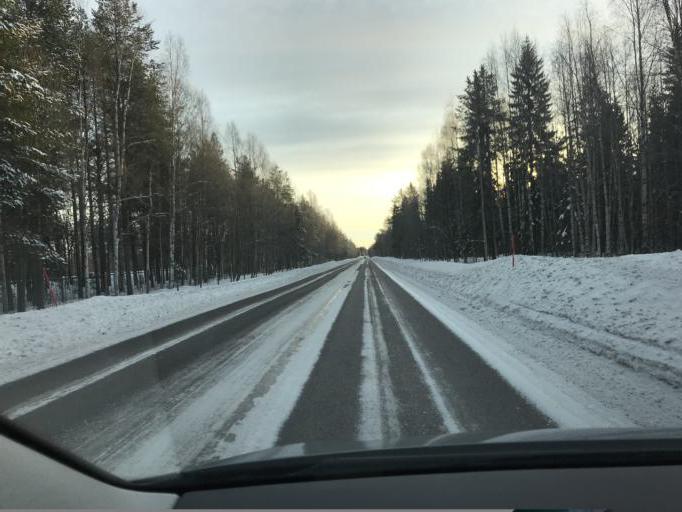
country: SE
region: Norrbotten
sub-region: Lulea Kommun
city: Bergnaset
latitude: 65.6199
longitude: 22.0765
